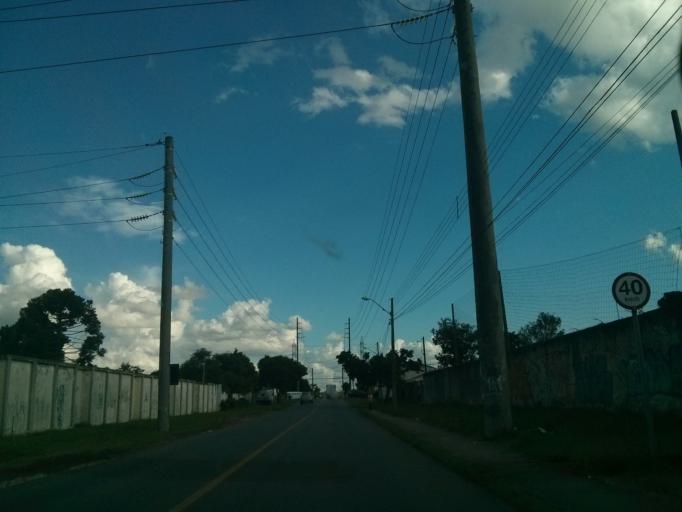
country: BR
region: Parana
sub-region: Sao Jose Dos Pinhais
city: Sao Jose dos Pinhais
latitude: -25.5228
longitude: -49.2298
